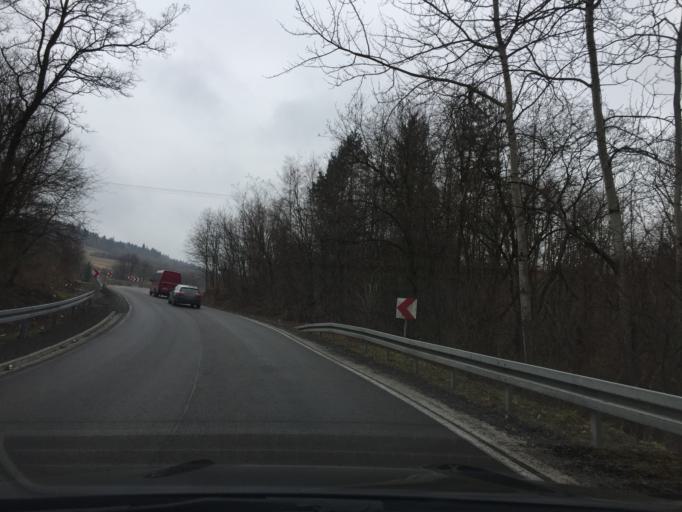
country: PL
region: Lesser Poland Voivodeship
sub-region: Powiat suski
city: Palcza
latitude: 49.8080
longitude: 19.7595
